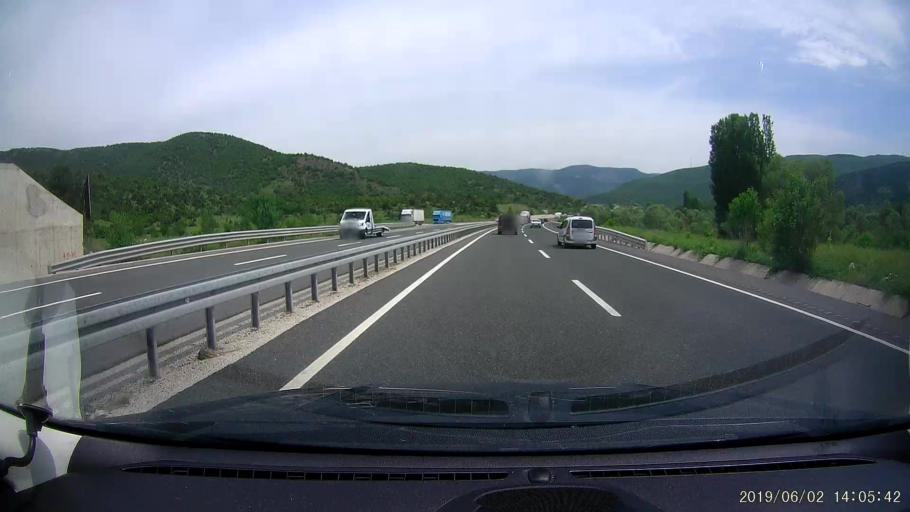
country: TR
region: Cankiri
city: Ilgaz
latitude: 40.8985
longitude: 33.6732
